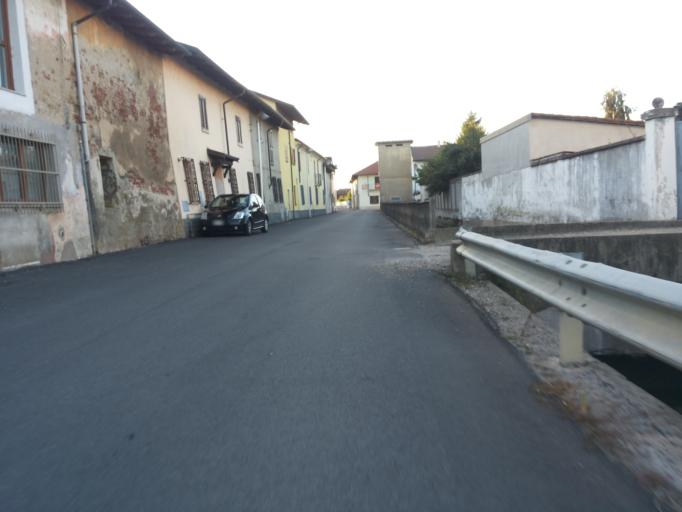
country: IT
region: Piedmont
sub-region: Provincia di Vercelli
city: Pezzana
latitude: 45.2622
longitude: 8.4899
